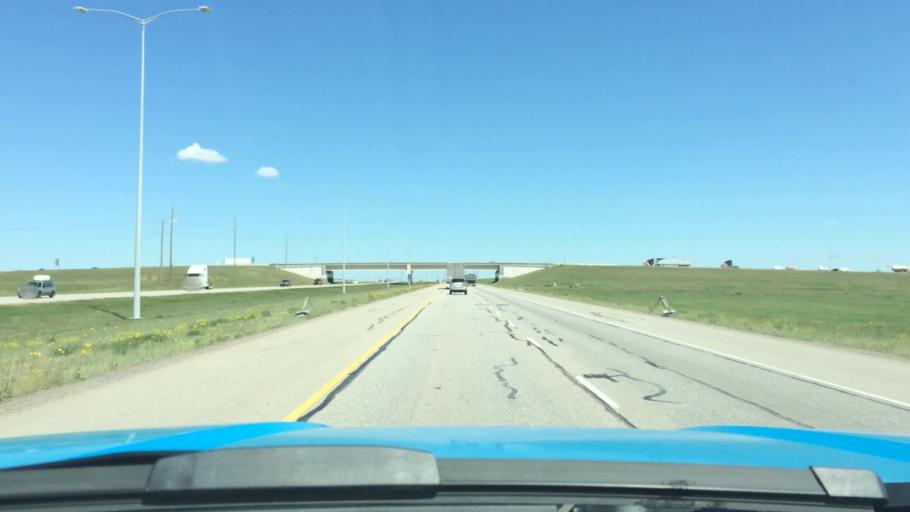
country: CA
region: Alberta
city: Chestermere
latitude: 51.0930
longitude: -113.9186
